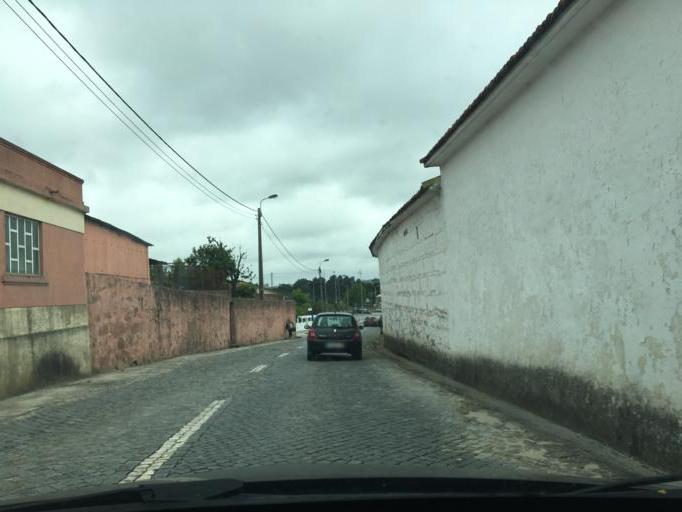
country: PT
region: Porto
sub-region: Matosinhos
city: Santa Cruz do Bispo
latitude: 41.2196
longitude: -8.6721
